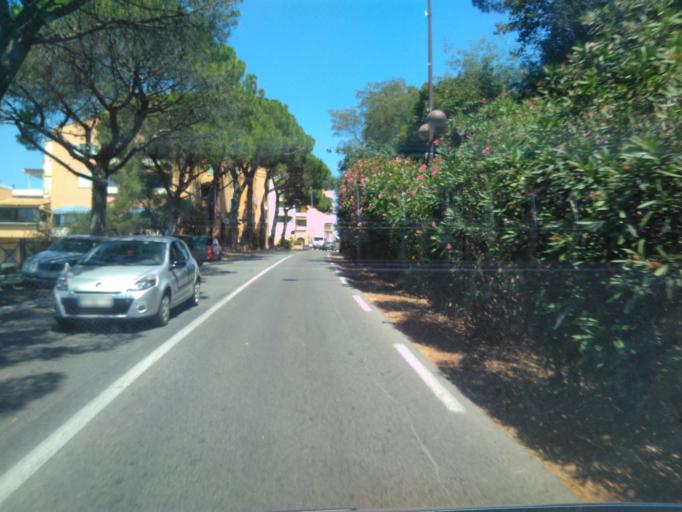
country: FR
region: Provence-Alpes-Cote d'Azur
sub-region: Departement du Var
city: La Croix-Valmer
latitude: 43.2075
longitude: 6.5691
